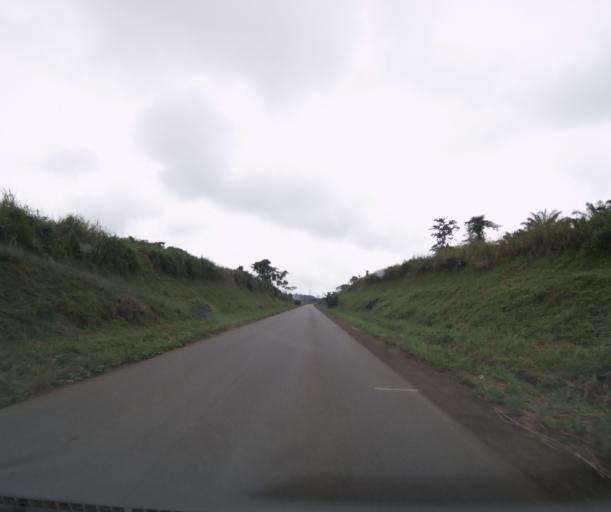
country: CM
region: Littoral
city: Edea
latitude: 3.6903
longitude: 10.1054
